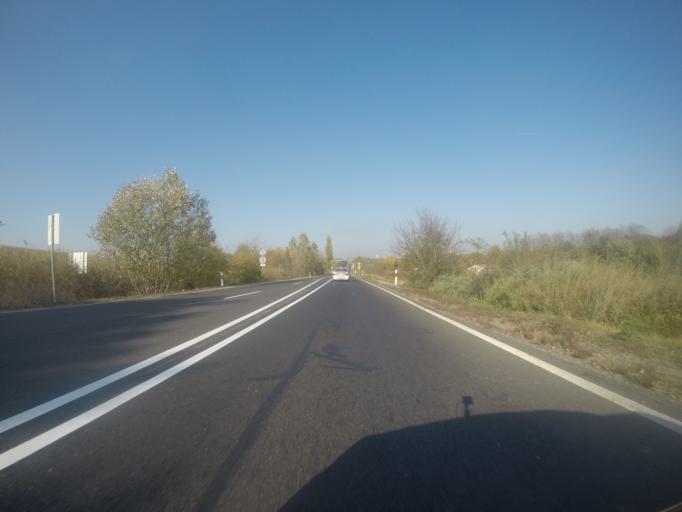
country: HU
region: Fejer
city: Baracs
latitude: 46.9025
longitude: 18.9241
